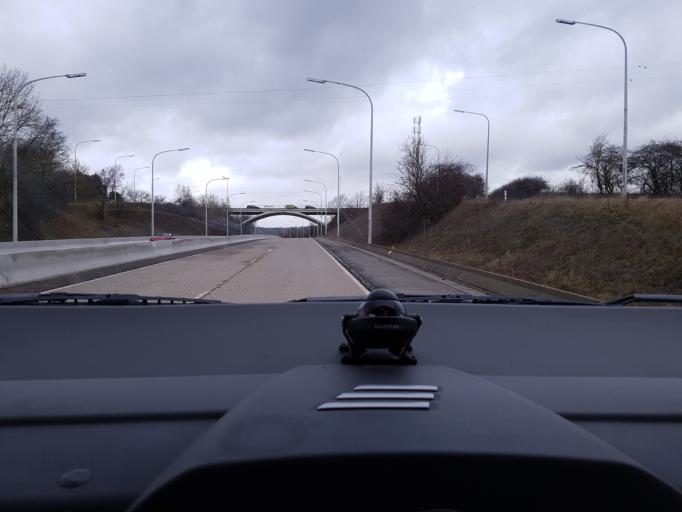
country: BE
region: Wallonia
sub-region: Province de Namur
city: Hamois
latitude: 50.2744
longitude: 5.2375
